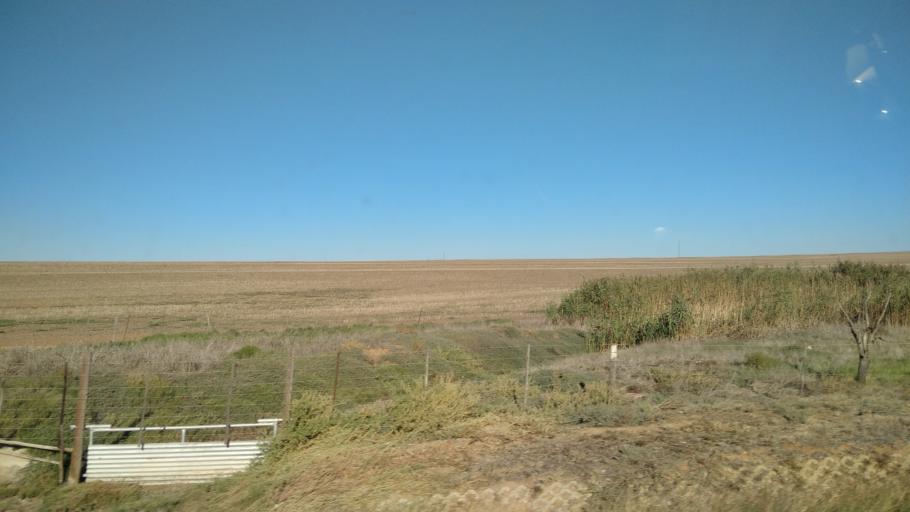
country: ZA
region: Western Cape
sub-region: West Coast District Municipality
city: Malmesbury
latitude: -33.3479
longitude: 18.6400
